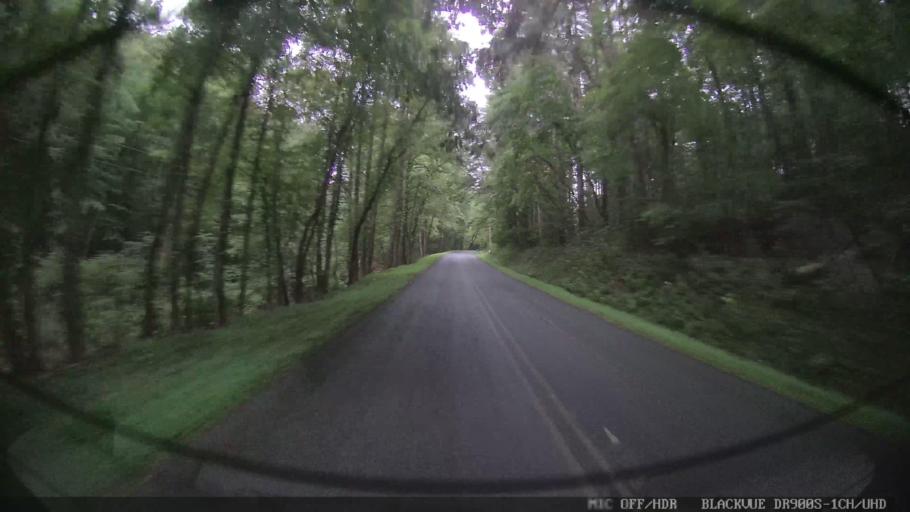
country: US
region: Georgia
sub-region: Gilmer County
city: Ellijay
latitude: 34.7777
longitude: -84.5417
